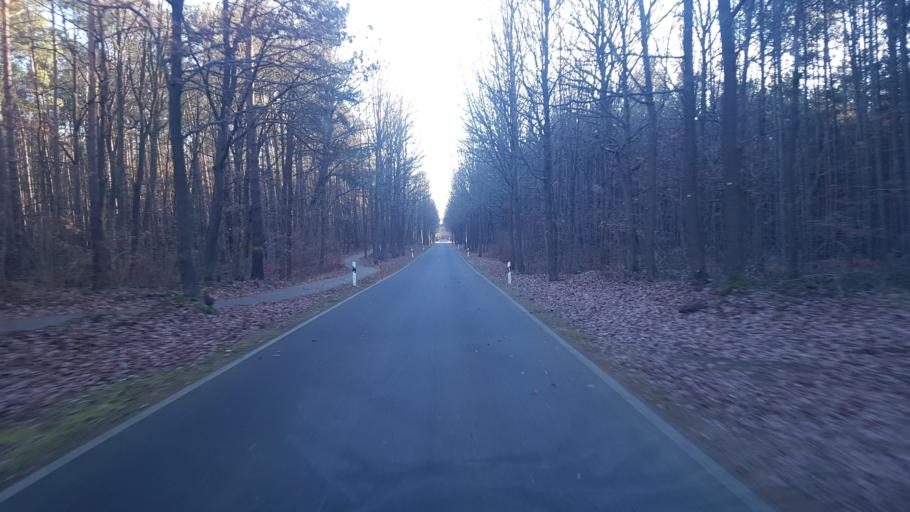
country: DE
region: Brandenburg
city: Tauer
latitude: 51.9241
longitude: 14.4887
